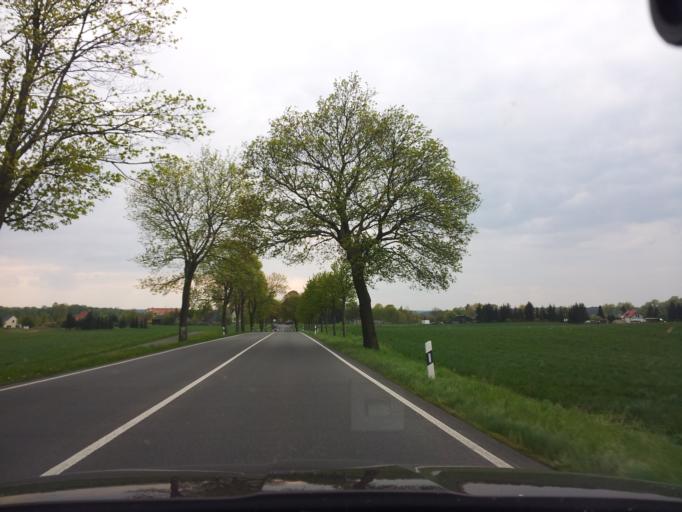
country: DE
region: Brandenburg
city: Lietzen
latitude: 52.5135
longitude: 14.3356
